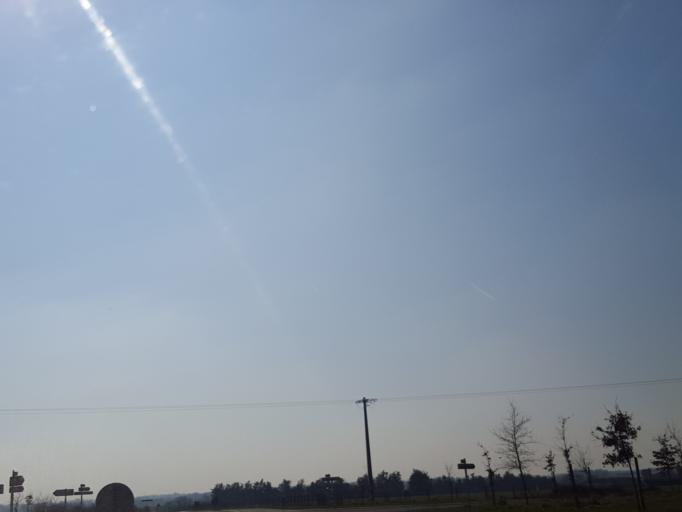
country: FR
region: Pays de la Loire
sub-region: Departement de la Vendee
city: Saint-Fulgent
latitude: 46.8559
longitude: -1.1919
